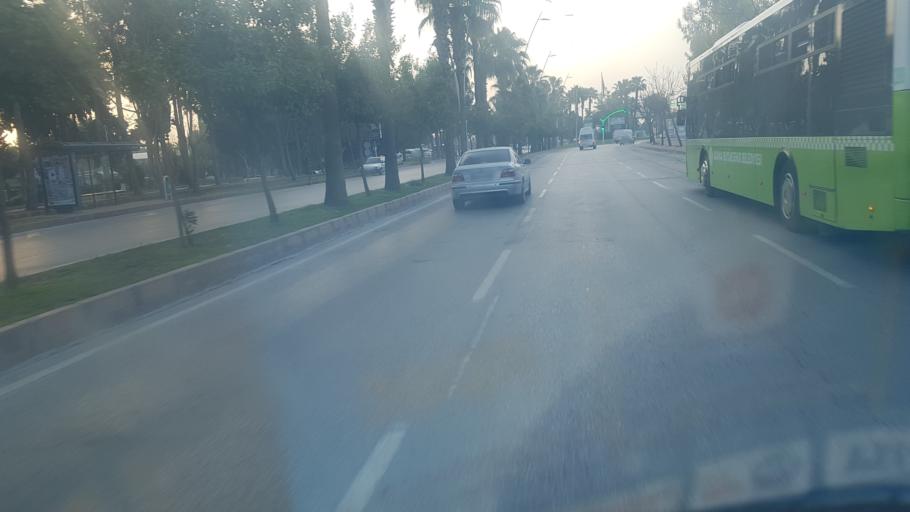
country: TR
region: Adana
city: Adana
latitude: 37.0098
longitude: 35.3311
